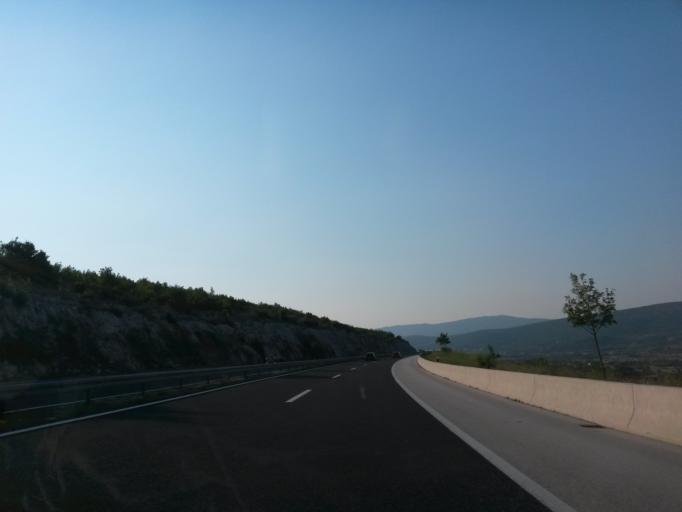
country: HR
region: Splitsko-Dalmatinska
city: Dugopolje
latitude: 43.5914
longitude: 16.6273
